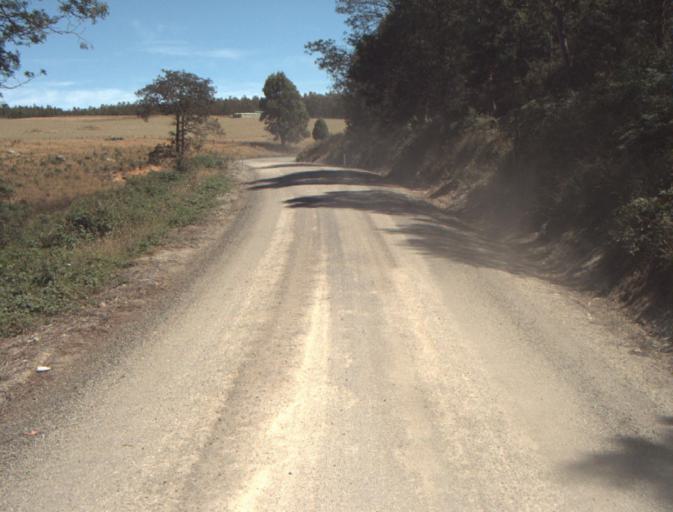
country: AU
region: Tasmania
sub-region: Dorset
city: Scottsdale
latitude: -41.3223
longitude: 147.4507
